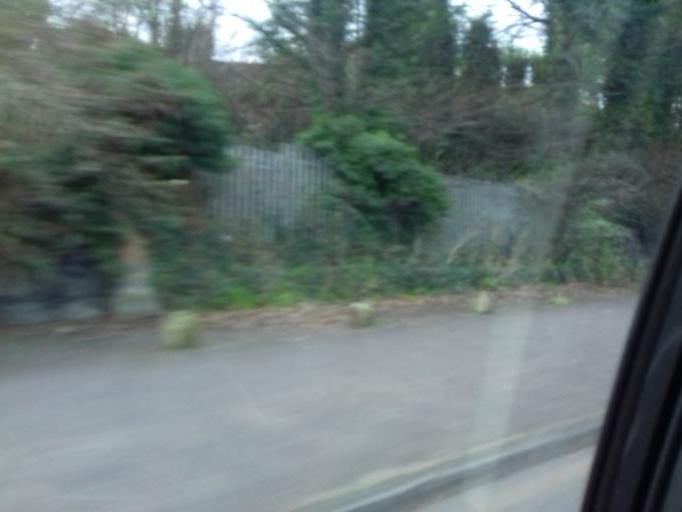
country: GB
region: Northern Ireland
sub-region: Newtownabbey District
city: Newtownabbey
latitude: 54.6290
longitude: -5.9241
